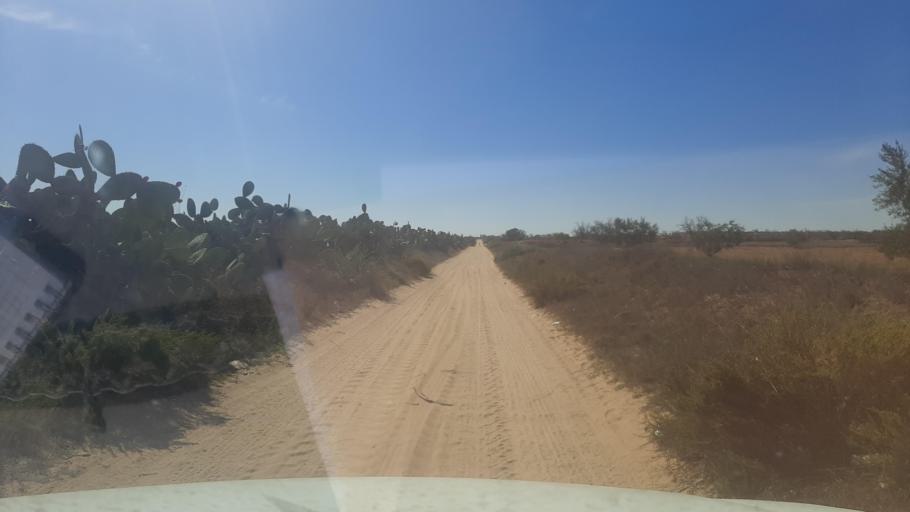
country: TN
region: Safaqis
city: Sfax
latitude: 34.8407
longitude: 10.5595
